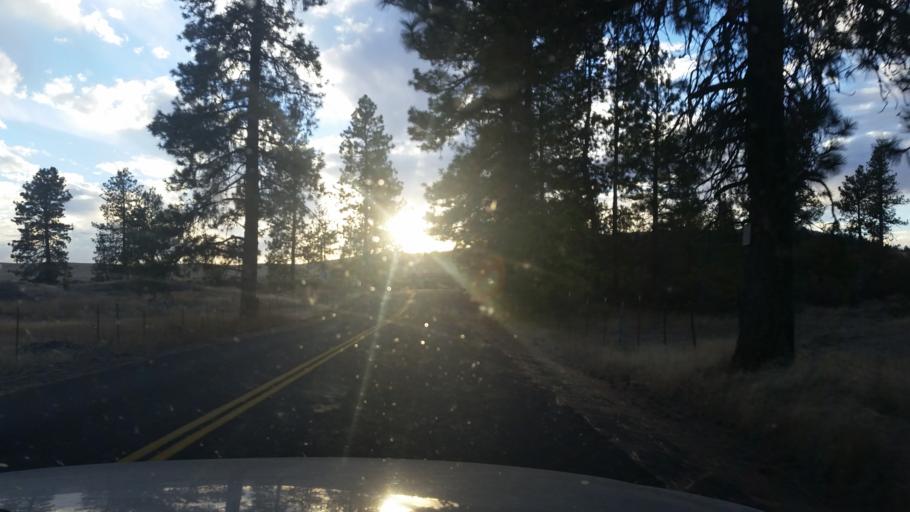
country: US
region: Washington
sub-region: Spokane County
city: Medical Lake
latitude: 47.5475
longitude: -117.7023
